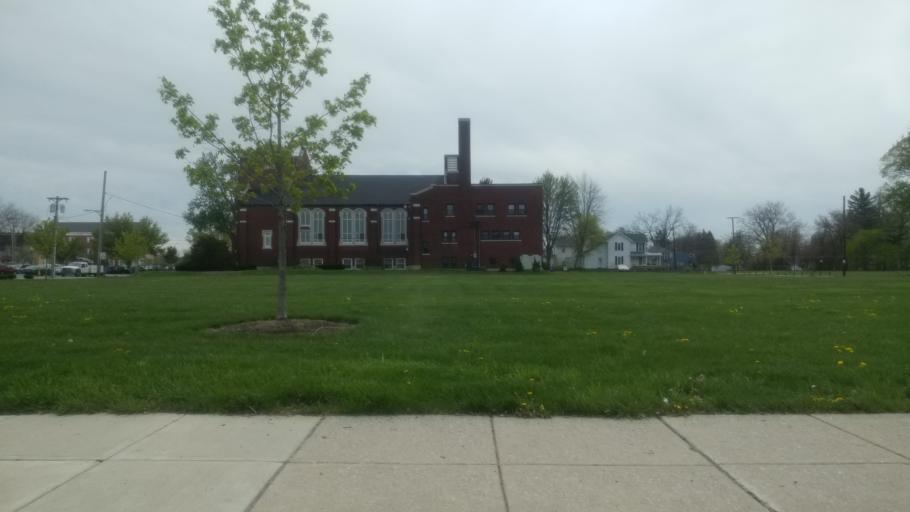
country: US
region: Ohio
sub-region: Wood County
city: Bowling Green
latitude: 41.3749
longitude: -83.6526
